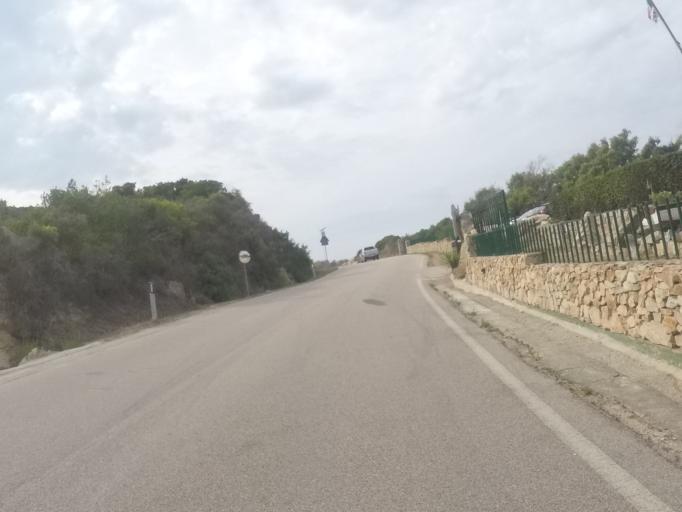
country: IT
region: Sardinia
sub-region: Provincia di Olbia-Tempio
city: Palau
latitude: 41.1753
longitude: 9.3992
